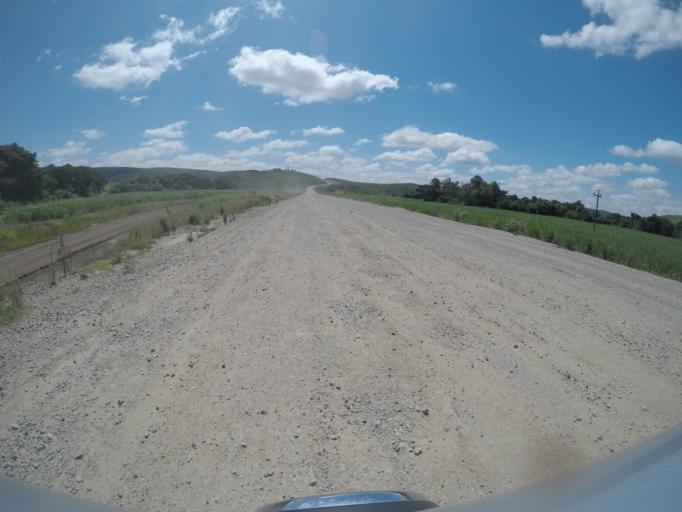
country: ZA
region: KwaZulu-Natal
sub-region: uThungulu District Municipality
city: Empangeni
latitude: -28.6460
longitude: 31.7671
